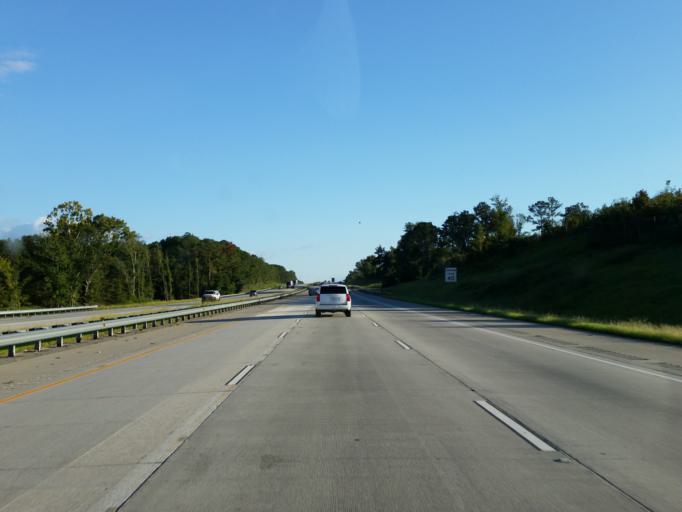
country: US
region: Georgia
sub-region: Dooly County
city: Unadilla
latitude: 32.3199
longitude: -83.7649
